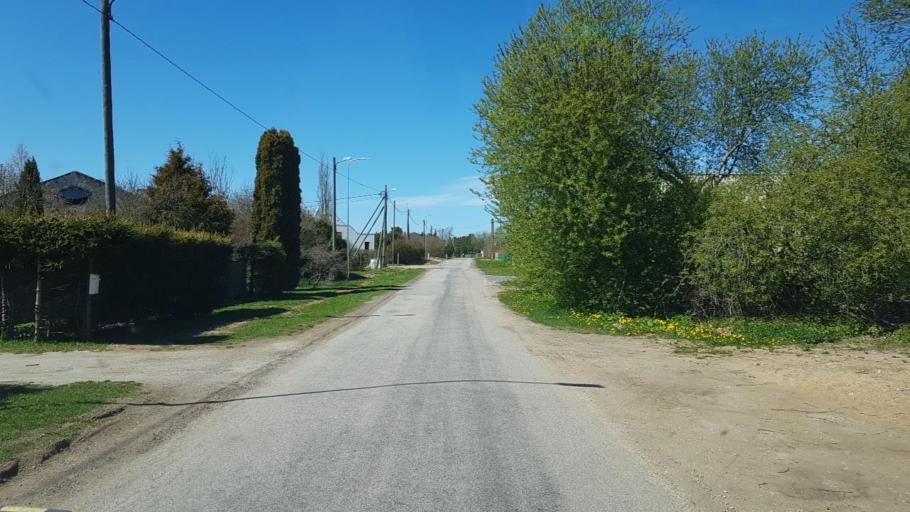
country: EE
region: Harju
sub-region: Viimsi vald
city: Viimsi
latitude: 59.4959
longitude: 24.8555
